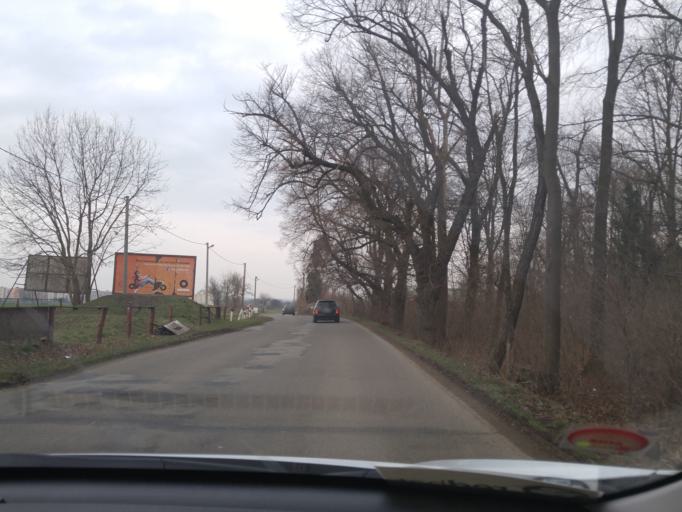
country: CZ
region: Central Bohemia
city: Neratovice
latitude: 50.2389
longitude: 14.5055
